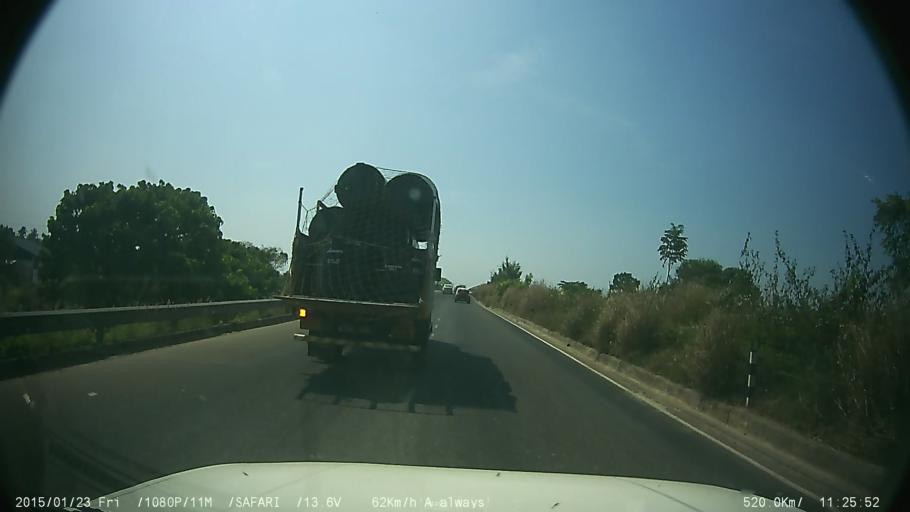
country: IN
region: Kerala
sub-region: Alappuzha
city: Arukutti
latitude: 9.9068
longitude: 76.3161
